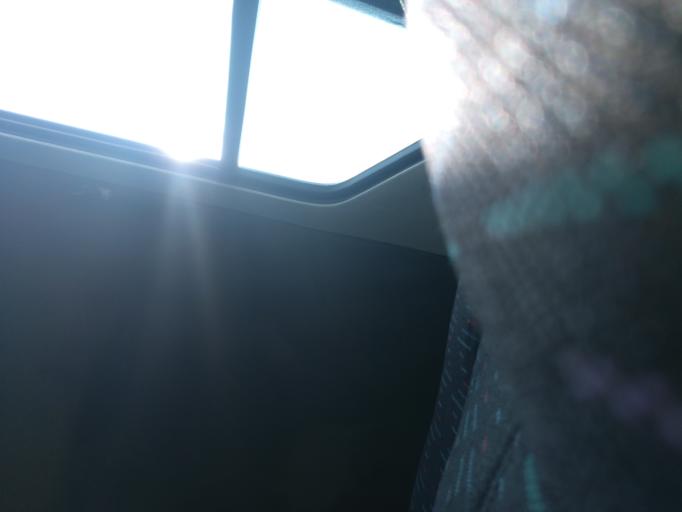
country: NG
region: Lagos
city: Lagos
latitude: 6.4567
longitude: 3.4085
